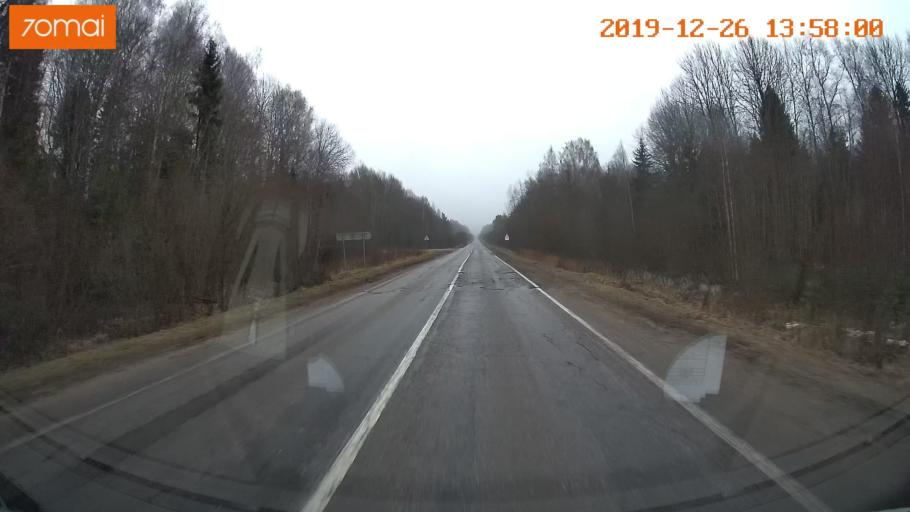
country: RU
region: Jaroslavl
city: Poshekhon'ye
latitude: 58.5777
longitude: 38.6913
